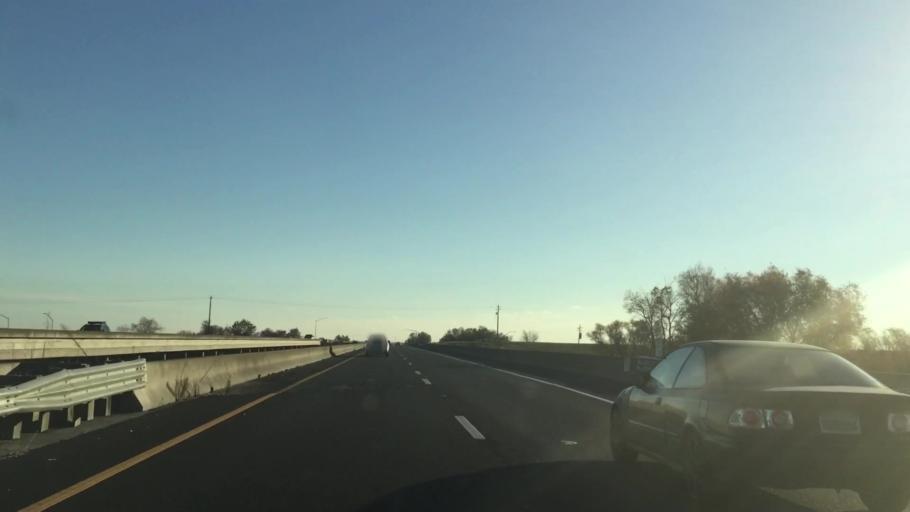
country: US
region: California
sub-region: Sacramento County
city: Elverta
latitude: 38.8225
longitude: -121.5438
